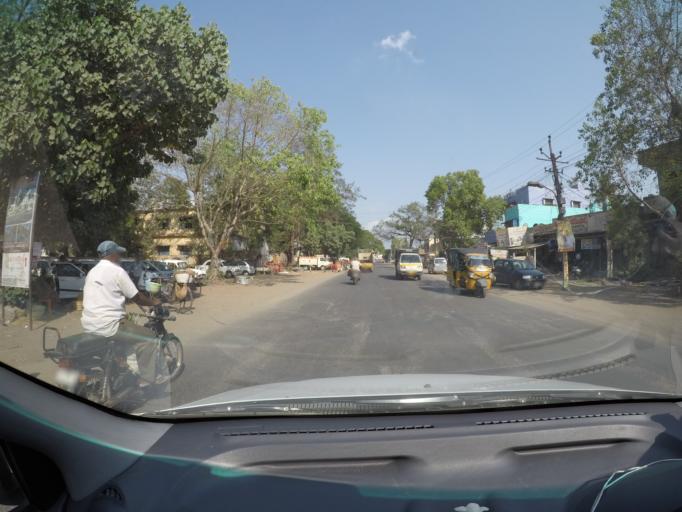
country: IN
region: Andhra Pradesh
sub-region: Krishna
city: Kankipadu
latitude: 16.4356
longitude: 80.7662
